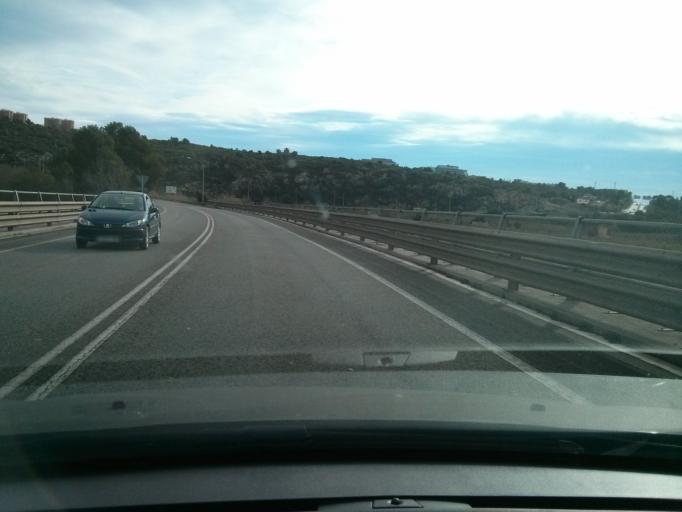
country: ES
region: Catalonia
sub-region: Provincia de Tarragona
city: Constanti
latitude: 41.1417
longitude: 1.2350
